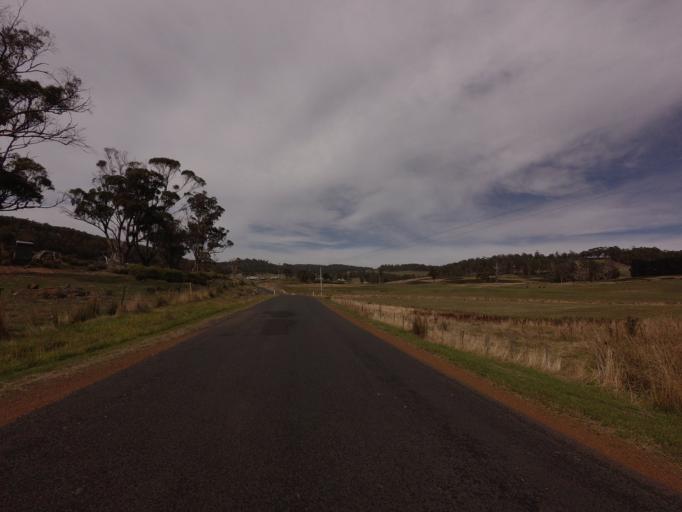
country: AU
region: Tasmania
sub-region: Sorell
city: Sorell
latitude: -42.4582
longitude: 147.5734
